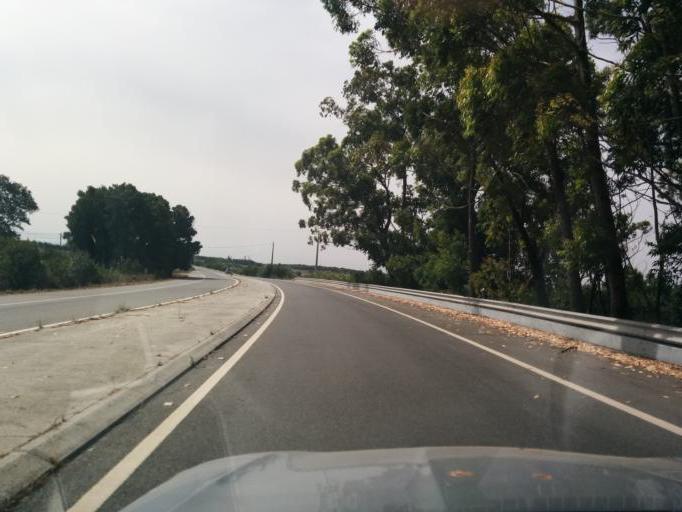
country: PT
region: Beja
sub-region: Odemira
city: Vila Nova de Milfontes
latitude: 37.7024
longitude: -8.7713
